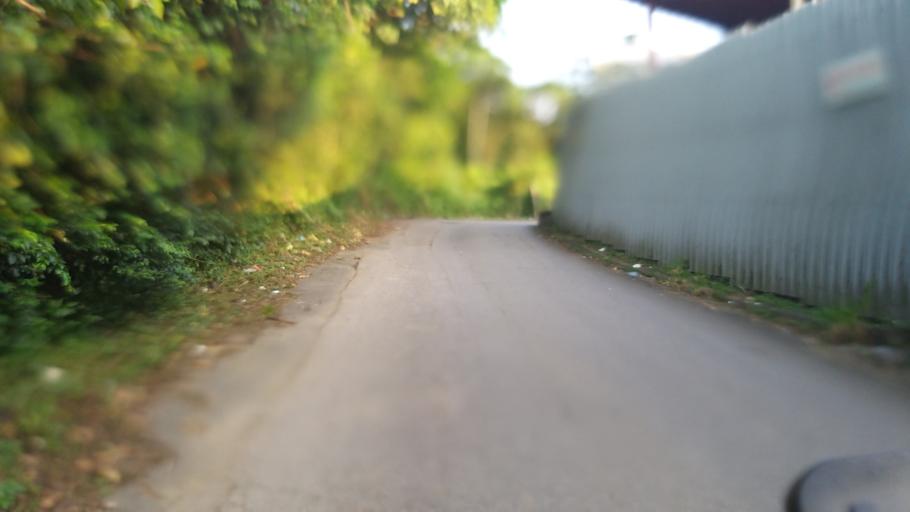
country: HK
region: Yuen Long
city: Yuen Long Kau Hui
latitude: 22.4457
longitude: 114.0140
